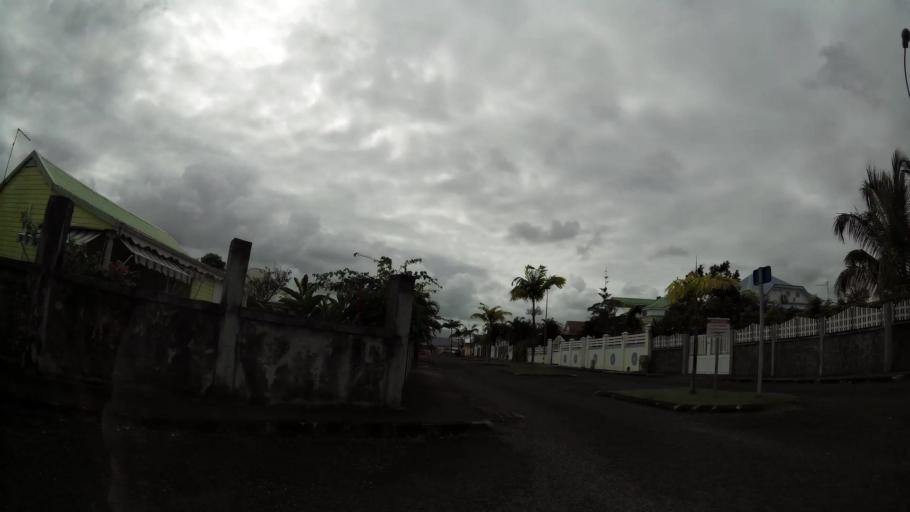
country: GP
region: Guadeloupe
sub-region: Guadeloupe
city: Lamentin
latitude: 16.2618
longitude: -61.6248
